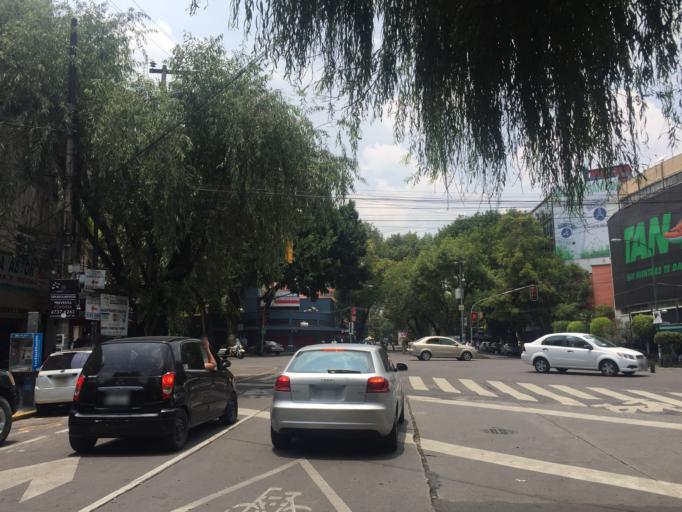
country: MX
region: Mexico City
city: Benito Juarez
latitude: 19.4115
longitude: -99.1735
